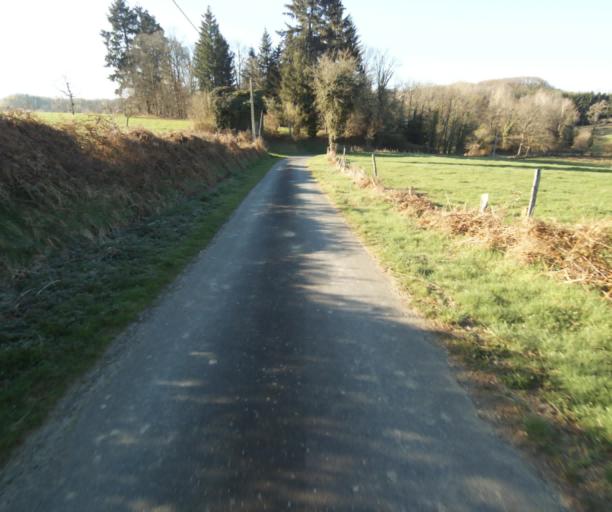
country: FR
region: Limousin
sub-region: Departement de la Correze
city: Uzerche
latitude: 45.3764
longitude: 1.5796
